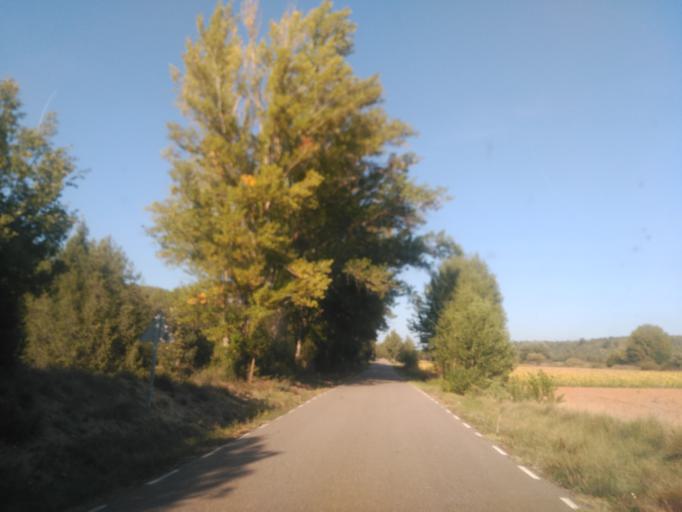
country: ES
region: Castille and Leon
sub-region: Provincia de Burgos
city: Brazacorta
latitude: 41.6977
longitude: -3.3999
